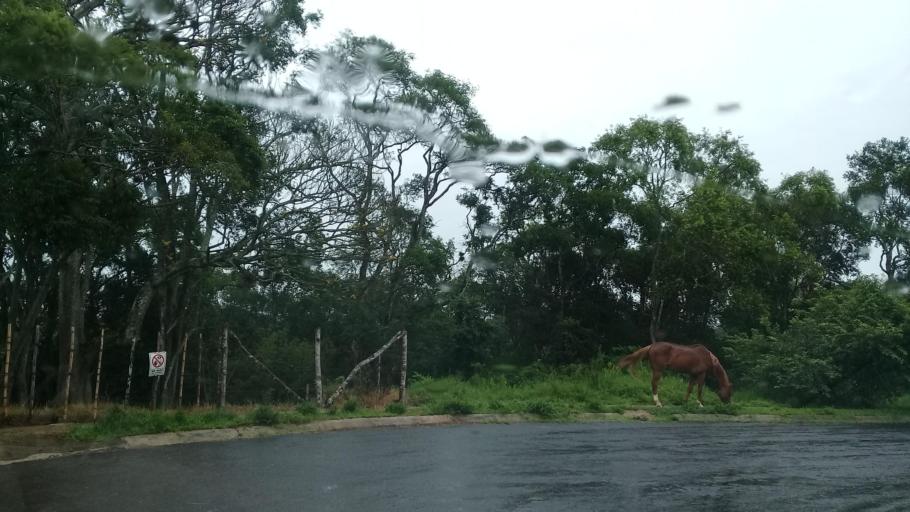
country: MX
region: Veracruz
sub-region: Xalapa
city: Lomas Verdes
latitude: 19.5151
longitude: -96.9003
